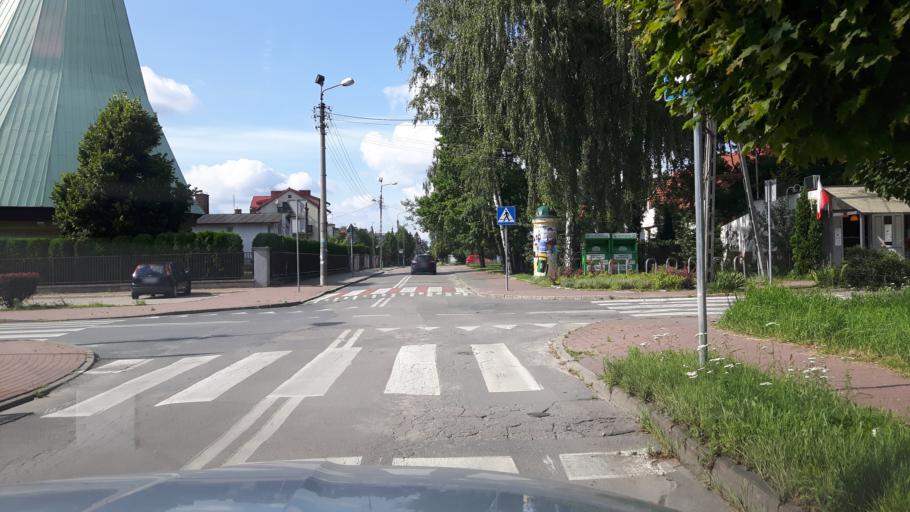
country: PL
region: Masovian Voivodeship
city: Zielonka
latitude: 52.2947
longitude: 21.1596
